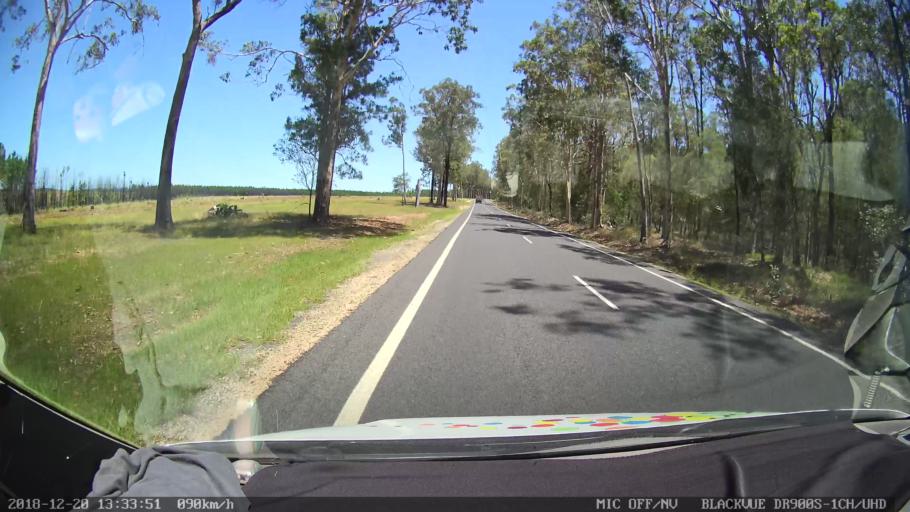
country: AU
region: New South Wales
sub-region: Clarence Valley
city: Gordon
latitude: -29.2511
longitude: 152.9851
